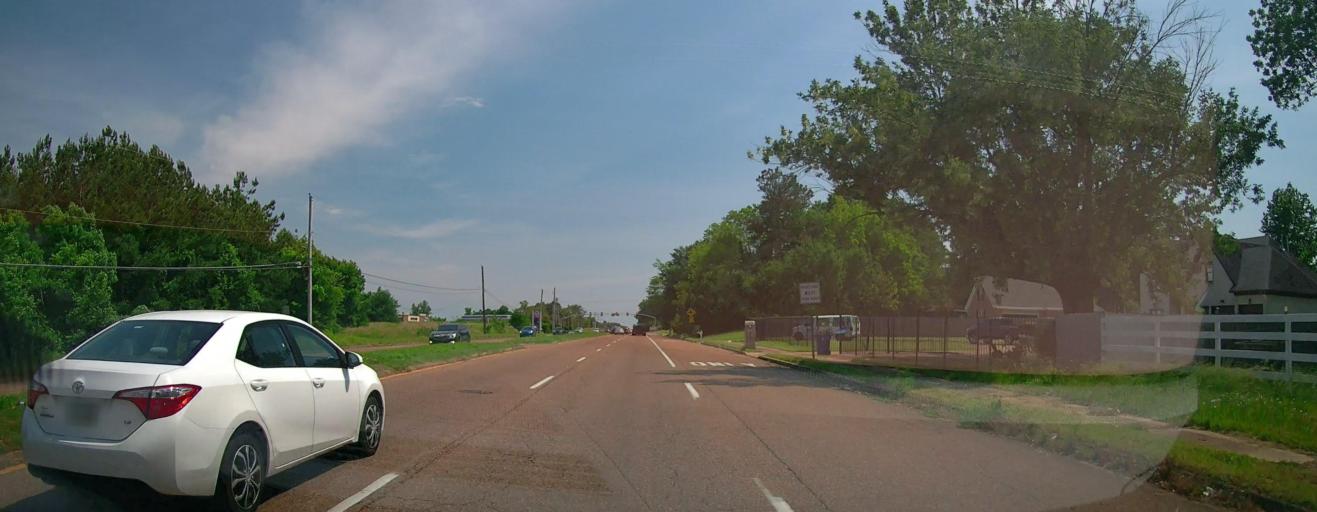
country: US
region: Mississippi
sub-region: De Soto County
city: Olive Branch
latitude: 34.9972
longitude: -89.8309
